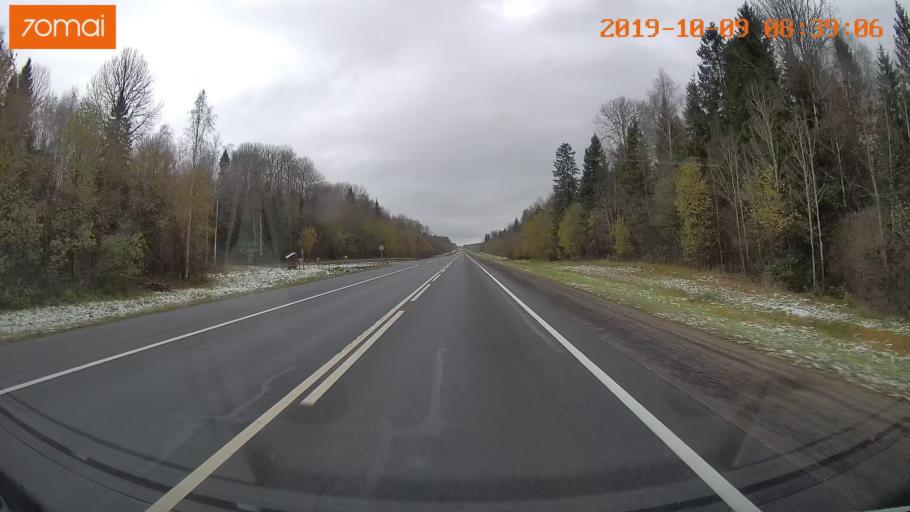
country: RU
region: Vologda
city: Gryazovets
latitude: 58.9664
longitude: 40.1574
